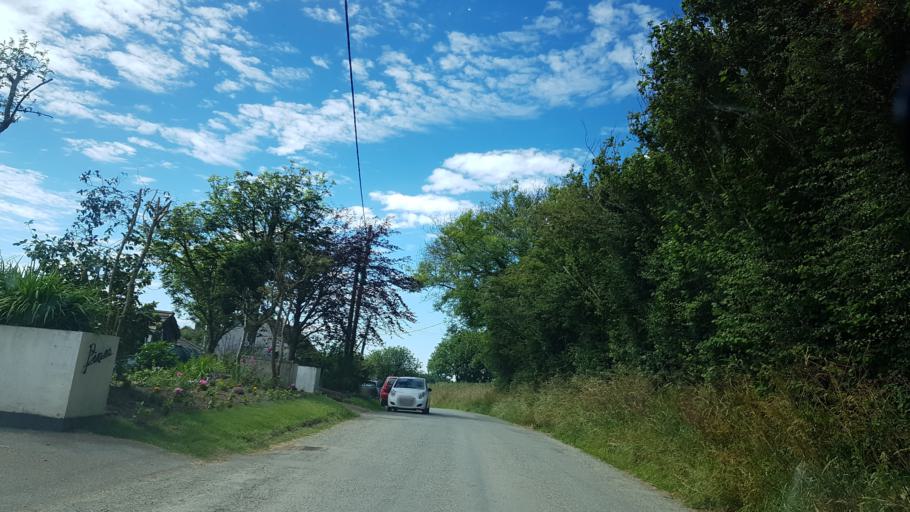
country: GB
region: Wales
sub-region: Pembrokeshire
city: Wiston
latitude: 51.8270
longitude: -4.8761
